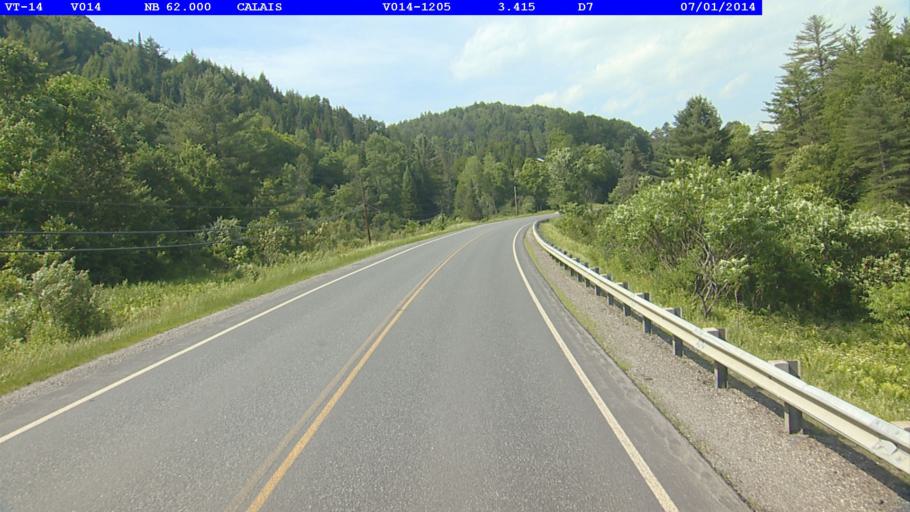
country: US
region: Vermont
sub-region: Washington County
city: Montpelier
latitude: 44.3549
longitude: -72.4451
